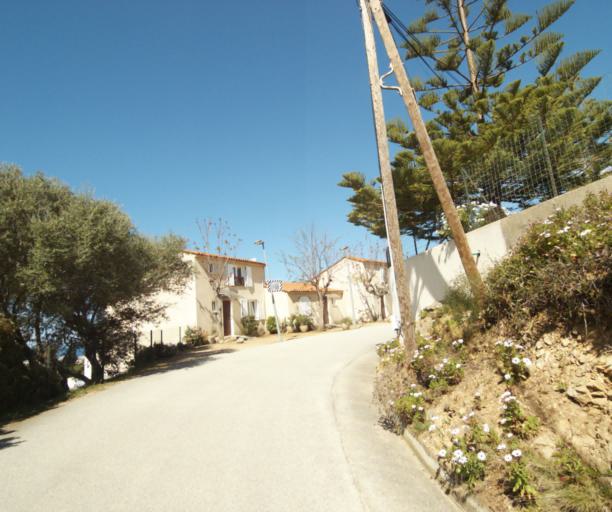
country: FR
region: Corsica
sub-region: Departement de la Corse-du-Sud
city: Propriano
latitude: 41.6796
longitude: 8.9158
